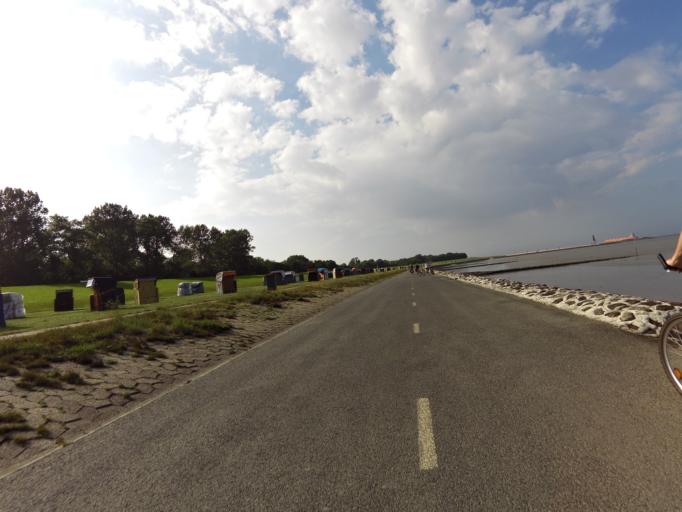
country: DE
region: Lower Saxony
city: Cuxhaven
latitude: 53.8826
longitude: 8.6845
